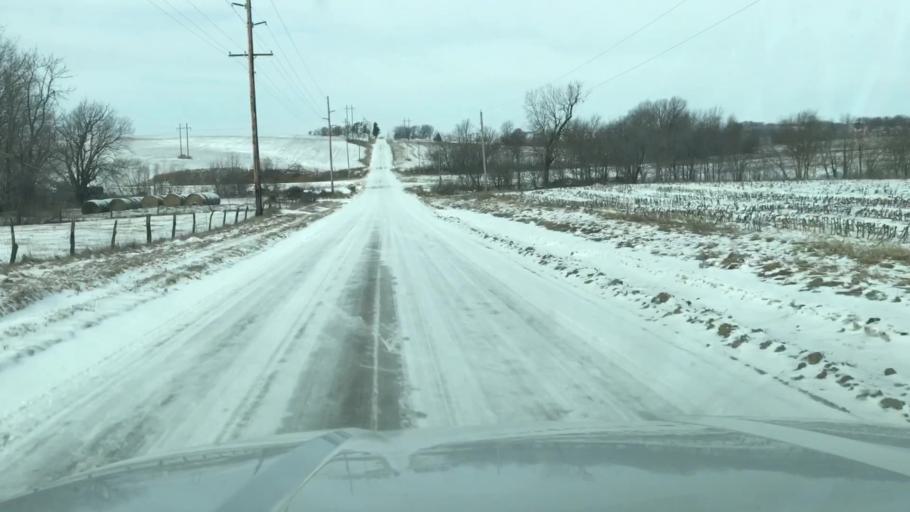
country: US
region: Missouri
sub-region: Holt County
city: Mound City
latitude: 40.1301
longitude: -95.0769
